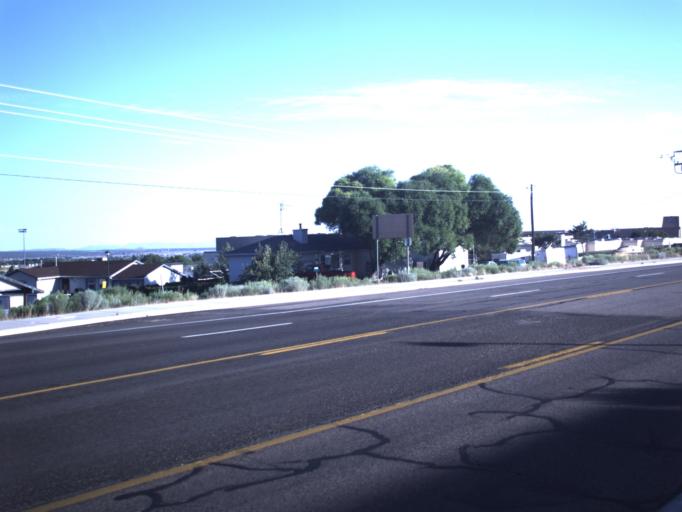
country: US
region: Utah
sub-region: Iron County
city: Cedar City
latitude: 37.7088
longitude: -113.0619
